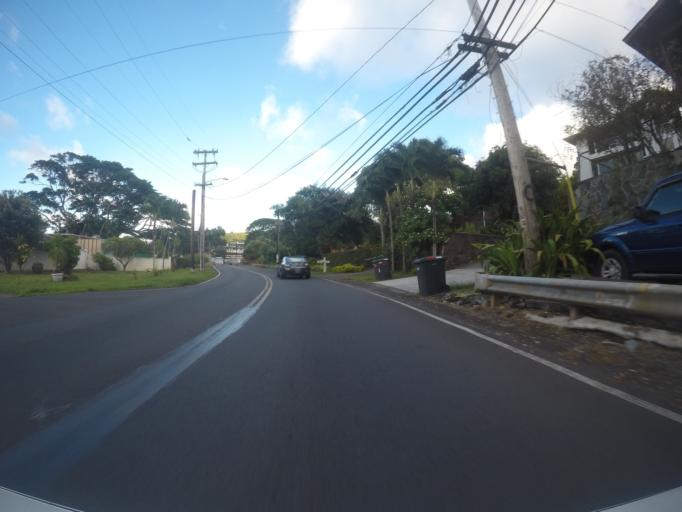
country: US
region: Hawaii
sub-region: Honolulu County
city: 'Ahuimanu
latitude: 21.4518
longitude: -157.8237
